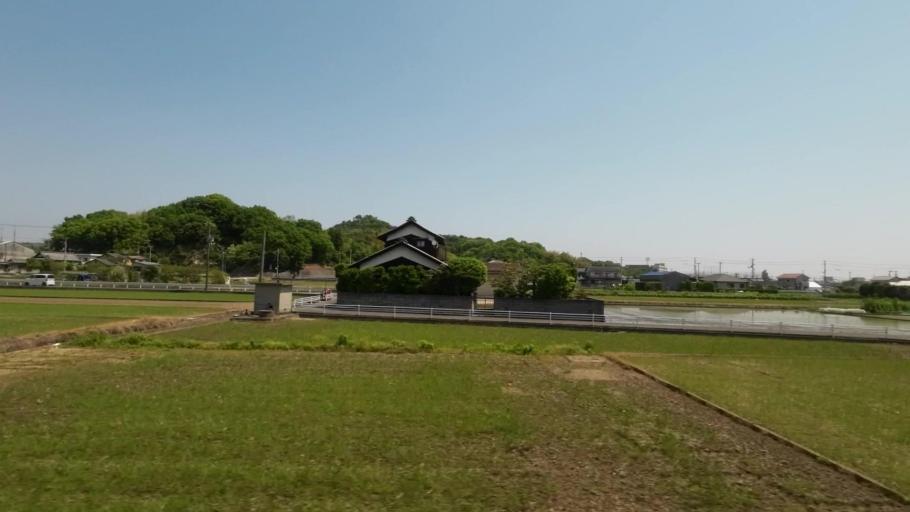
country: JP
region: Ehime
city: Saijo
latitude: 34.0208
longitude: 133.0272
